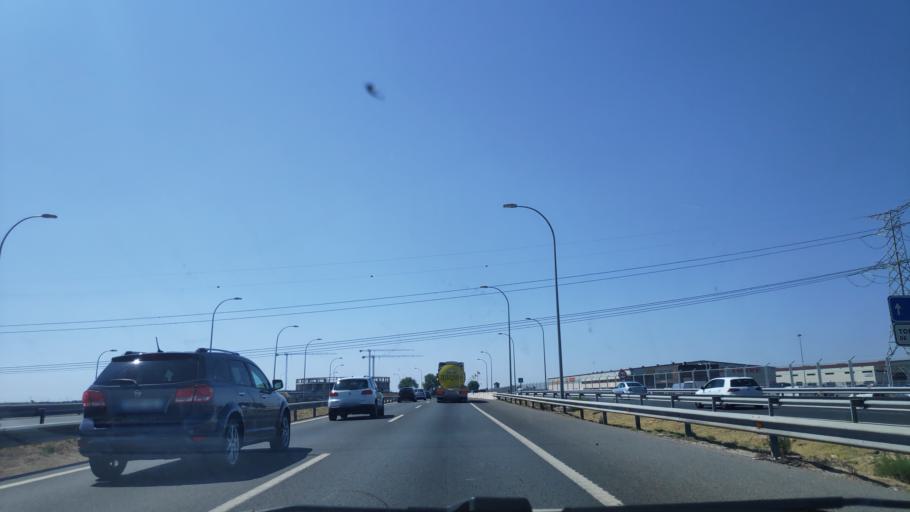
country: ES
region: Madrid
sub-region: Provincia de Madrid
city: Torrejon de la Calzada
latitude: 40.2140
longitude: -3.7899
